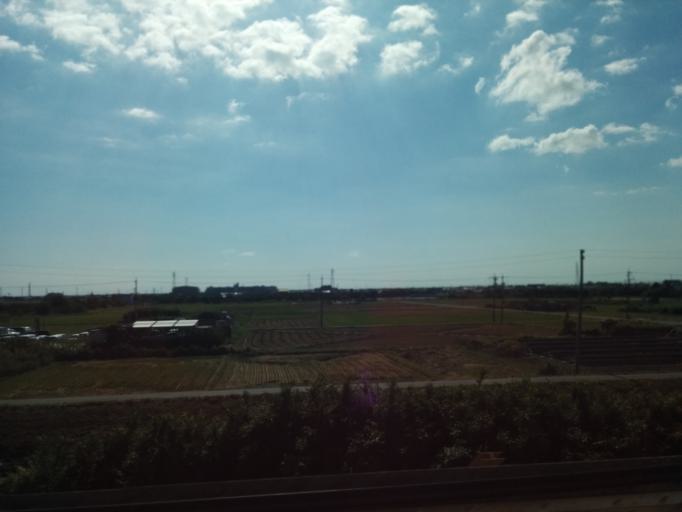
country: JP
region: Shizuoka
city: Iwata
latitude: 34.7067
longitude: 137.8575
